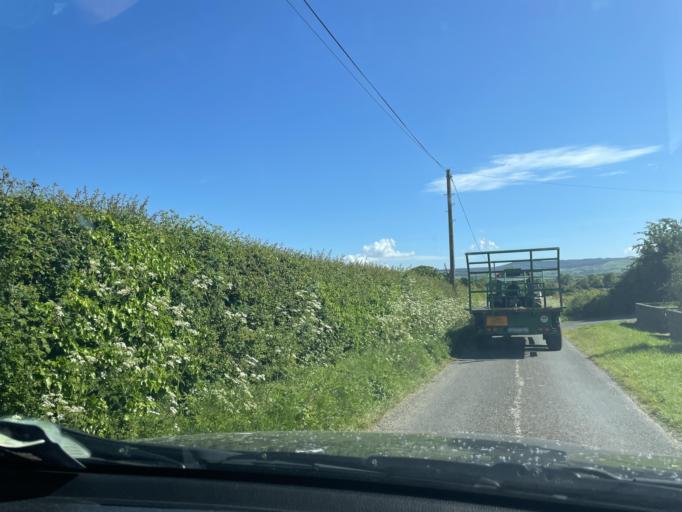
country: IE
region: Leinster
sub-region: County Carlow
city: Bagenalstown
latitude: 52.6323
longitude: -7.0153
